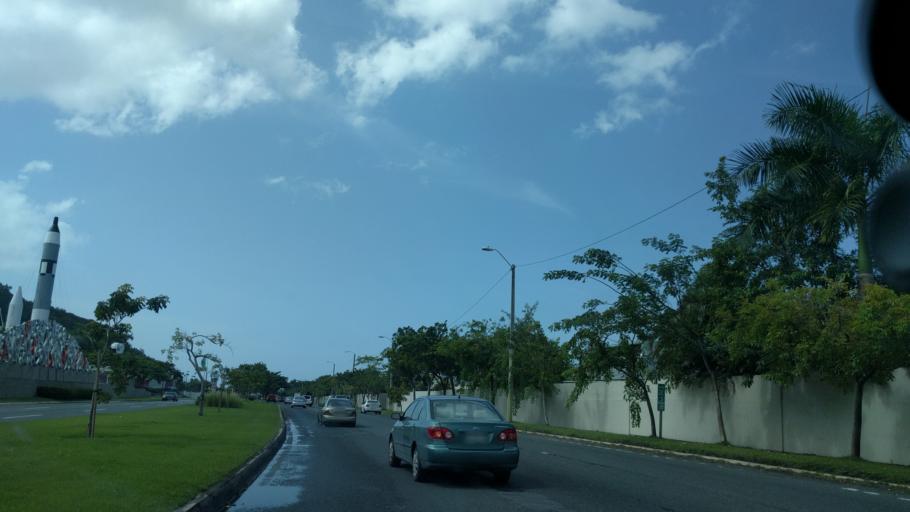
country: PR
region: Bayamon
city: Bayamon
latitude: 18.4100
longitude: -66.1590
